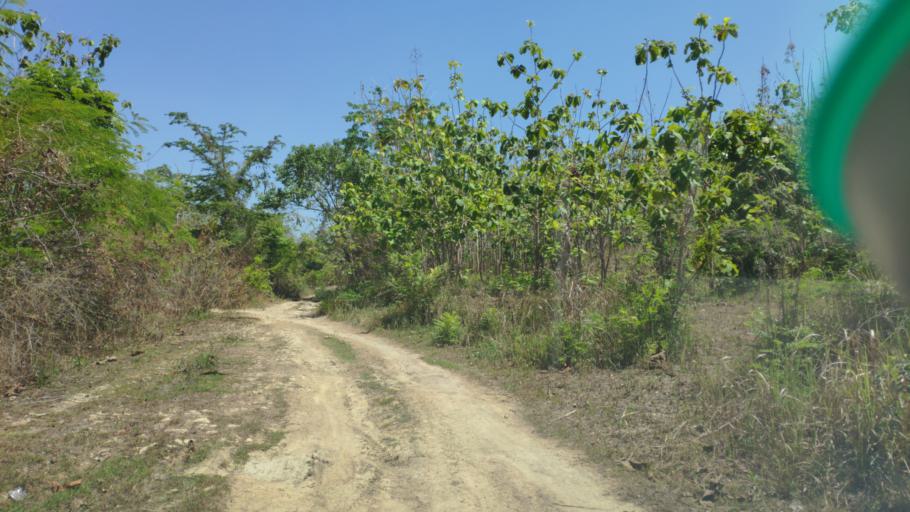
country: ID
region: Central Java
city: Suruhan
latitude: -7.0062
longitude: 111.5395
